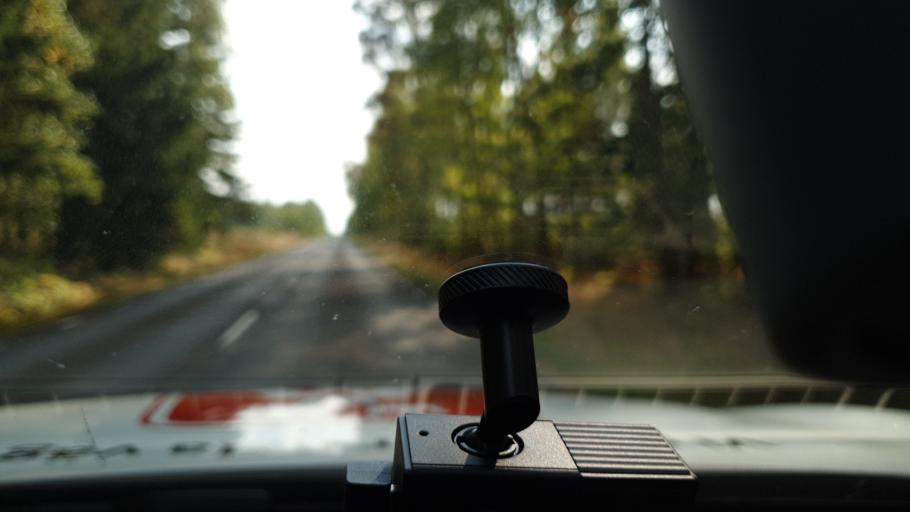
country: SE
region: Kalmar
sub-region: Vimmerby Kommun
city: Vimmerby
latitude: 57.7064
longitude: 15.8364
